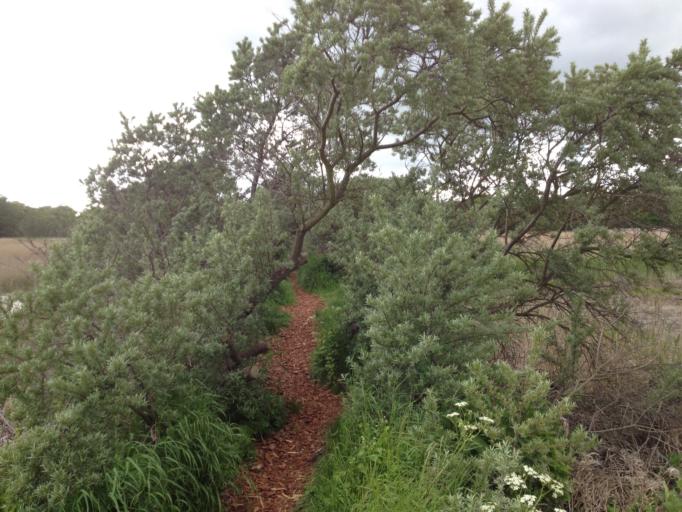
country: DK
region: Capital Region
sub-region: Fredensborg Kommune
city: Niva
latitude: 55.9289
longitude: 12.5222
